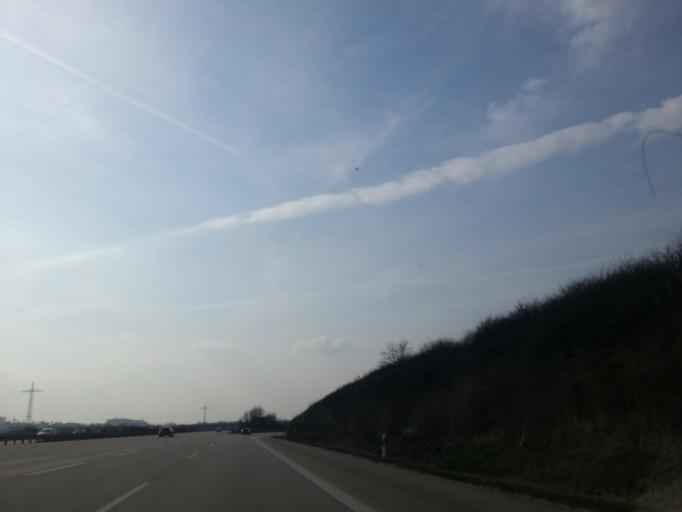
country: DE
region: Saxony
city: Radebeul
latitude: 51.0649
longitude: 13.6137
